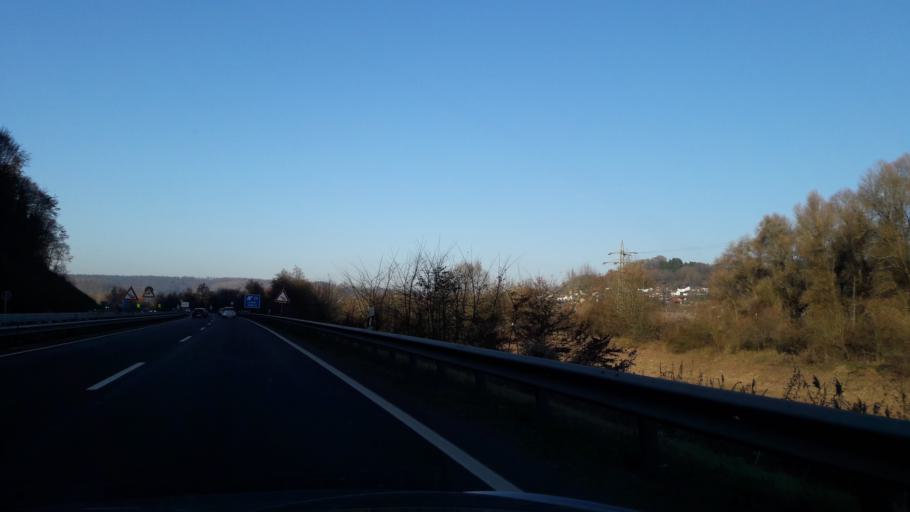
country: DE
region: Rheinland-Pfalz
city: Zweibrucken
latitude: 49.2580
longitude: 7.3282
